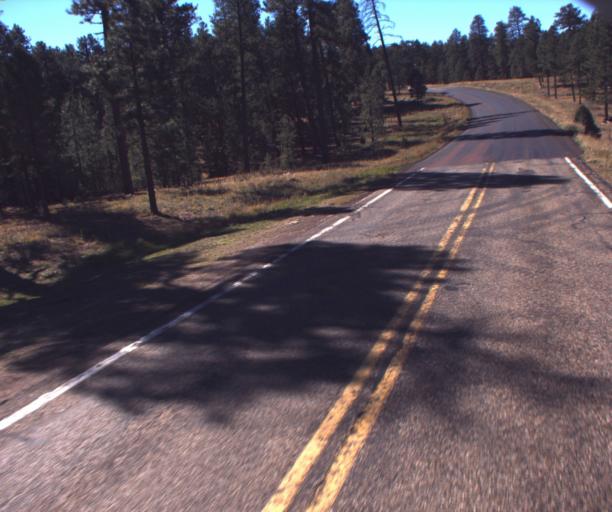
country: US
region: Arizona
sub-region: Coconino County
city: Fredonia
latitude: 36.7568
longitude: -112.2680
